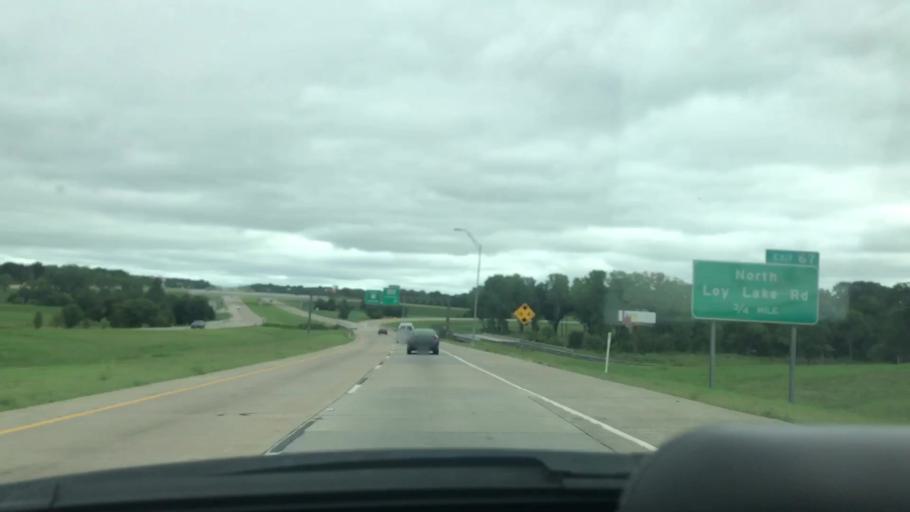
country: US
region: Texas
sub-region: Grayson County
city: Denison
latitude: 33.7150
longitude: -96.5857
